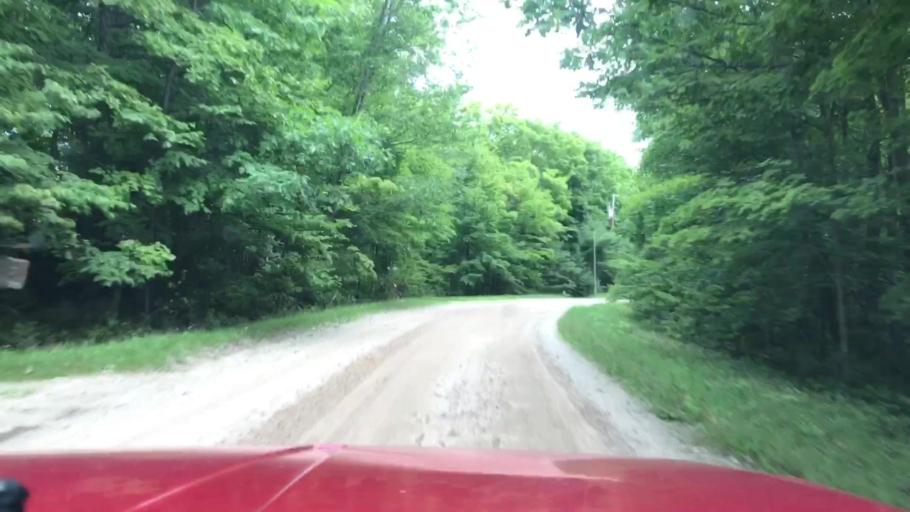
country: US
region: Michigan
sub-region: Charlevoix County
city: Charlevoix
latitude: 45.7282
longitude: -85.5665
